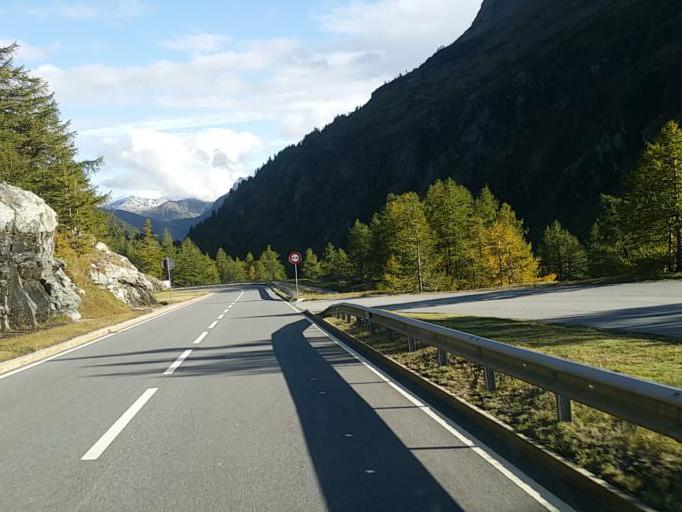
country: CH
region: Valais
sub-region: Brig District
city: Brig
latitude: 46.2254
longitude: 8.0161
